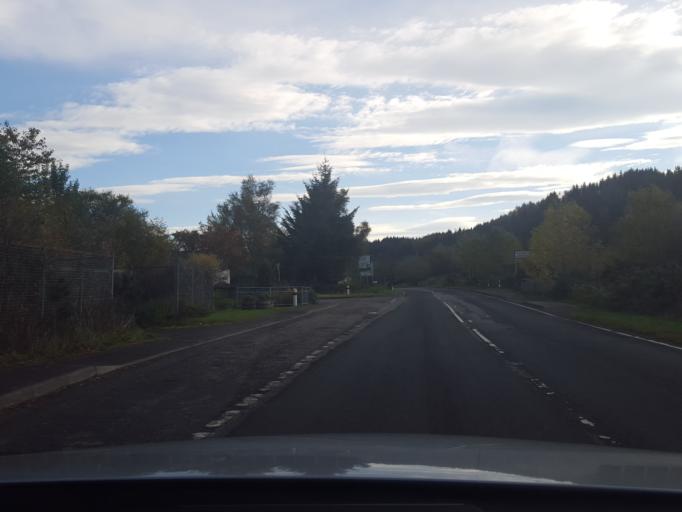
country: GB
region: Scotland
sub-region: Highland
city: Portree
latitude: 57.2859
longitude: -5.5875
